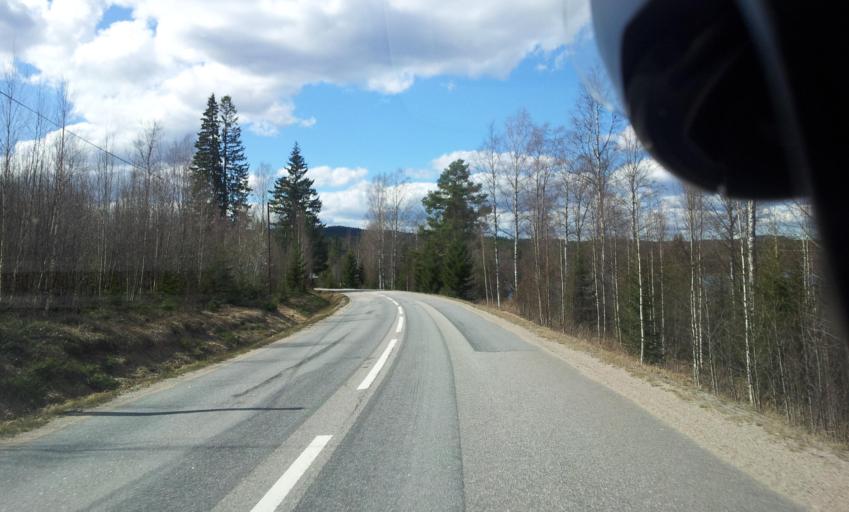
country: SE
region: Gaevleborg
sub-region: Ovanakers Kommun
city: Edsbyn
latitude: 61.3278
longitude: 15.8485
